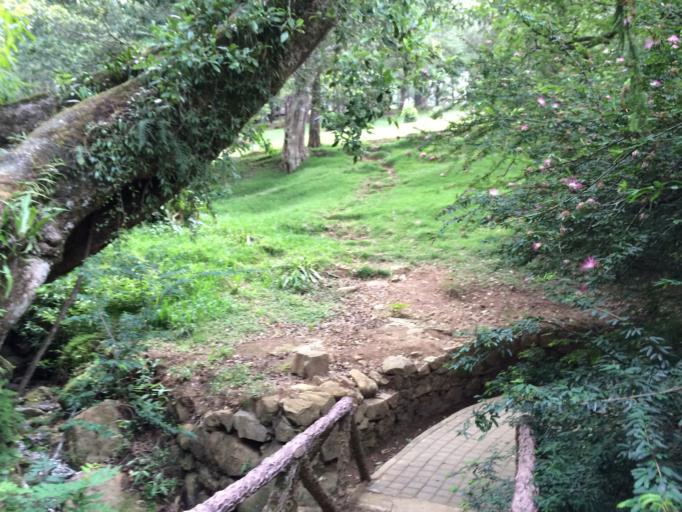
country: LK
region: Central
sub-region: Nuwara Eliya District
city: Nuwara Eliya
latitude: 6.9268
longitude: 80.8212
